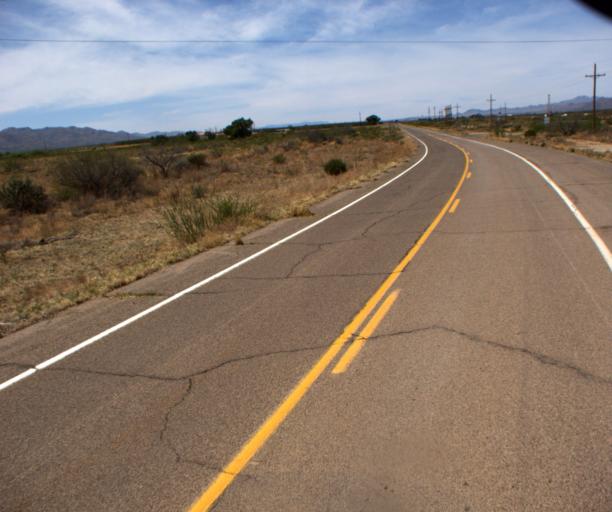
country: US
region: Arizona
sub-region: Cochise County
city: Willcox
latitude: 32.3202
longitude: -109.4526
